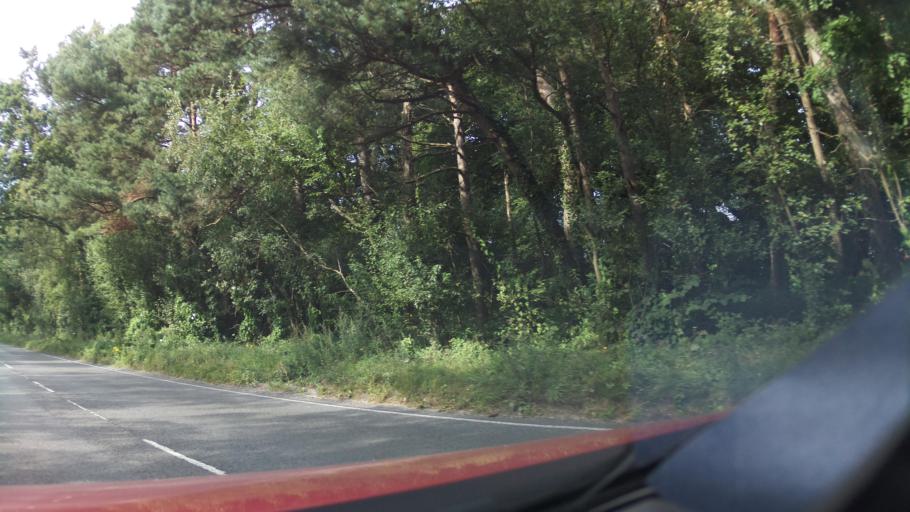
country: GB
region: England
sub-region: Hampshire
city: Hythe
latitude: 50.8604
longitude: -1.4311
